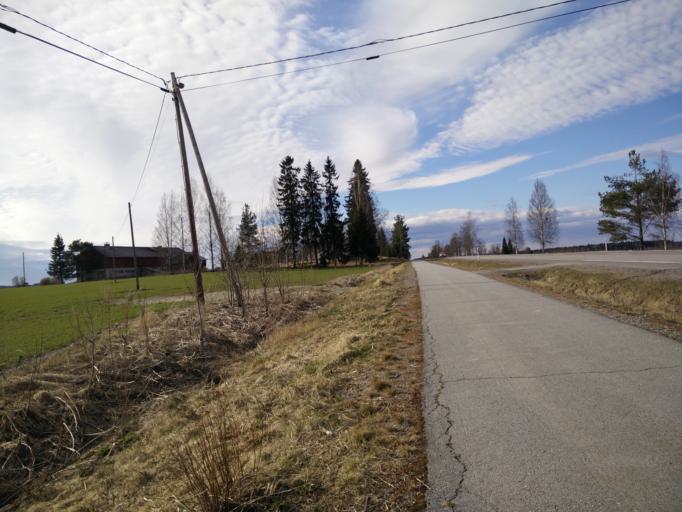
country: FI
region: Pirkanmaa
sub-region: Tampere
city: Orivesi
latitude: 61.7022
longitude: 24.3397
